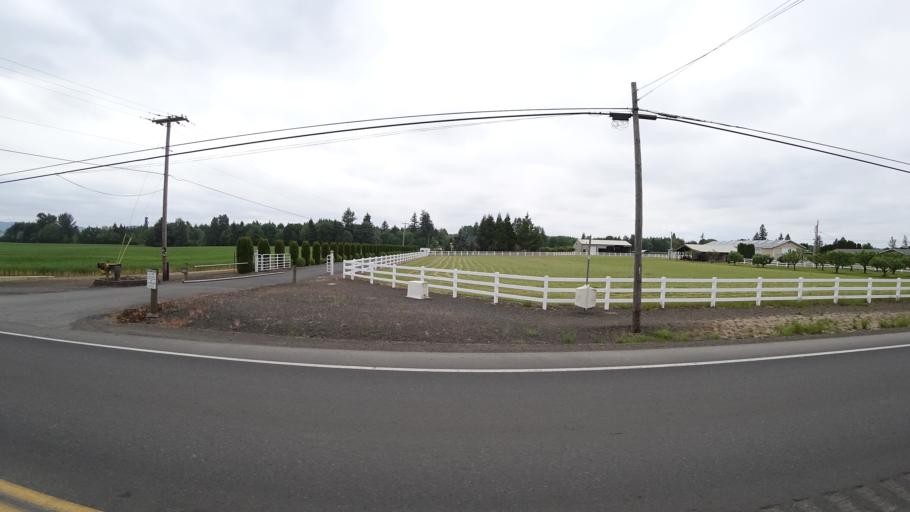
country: US
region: Oregon
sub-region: Washington County
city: Hillsboro
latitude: 45.4911
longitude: -122.9910
